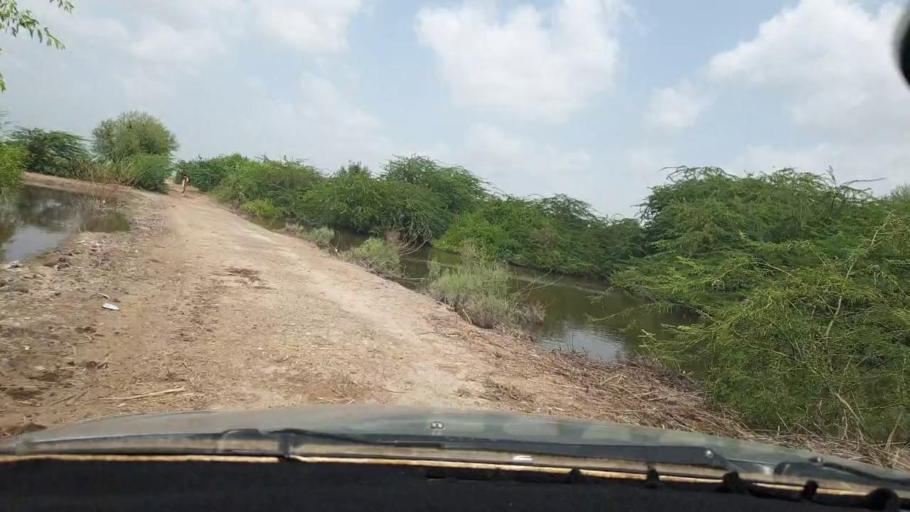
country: PK
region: Sindh
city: Tando Bago
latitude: 24.7601
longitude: 69.1685
